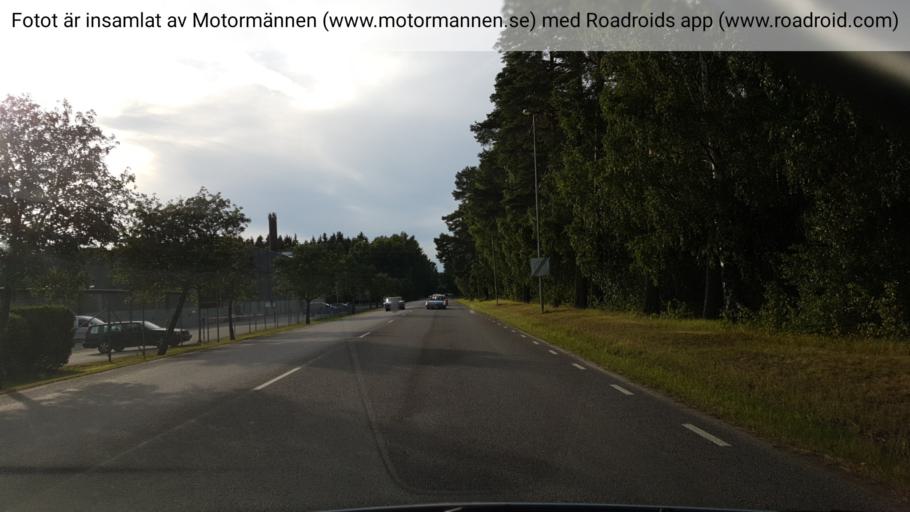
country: SE
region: Vaestra Goetaland
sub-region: Lidkopings Kommun
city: Lidkoping
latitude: 58.5137
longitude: 13.1368
